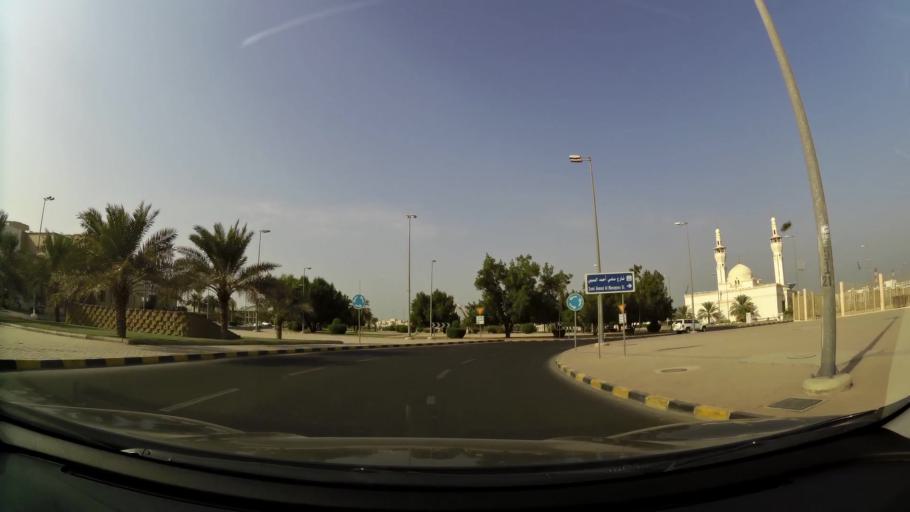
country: KW
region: Al Asimah
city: Ash Shamiyah
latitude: 29.3252
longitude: 47.9818
